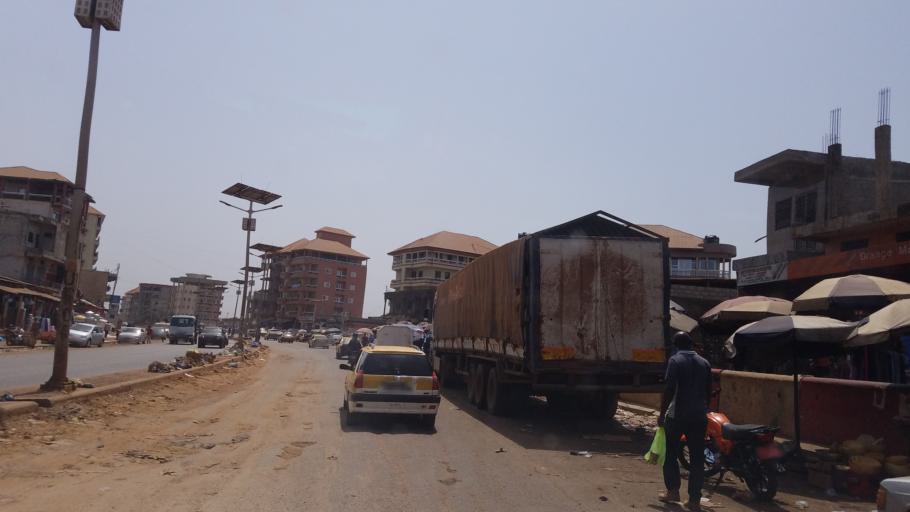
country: GN
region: Kindia
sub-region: Prefecture de Dubreka
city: Dubreka
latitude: 9.6657
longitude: -13.5620
